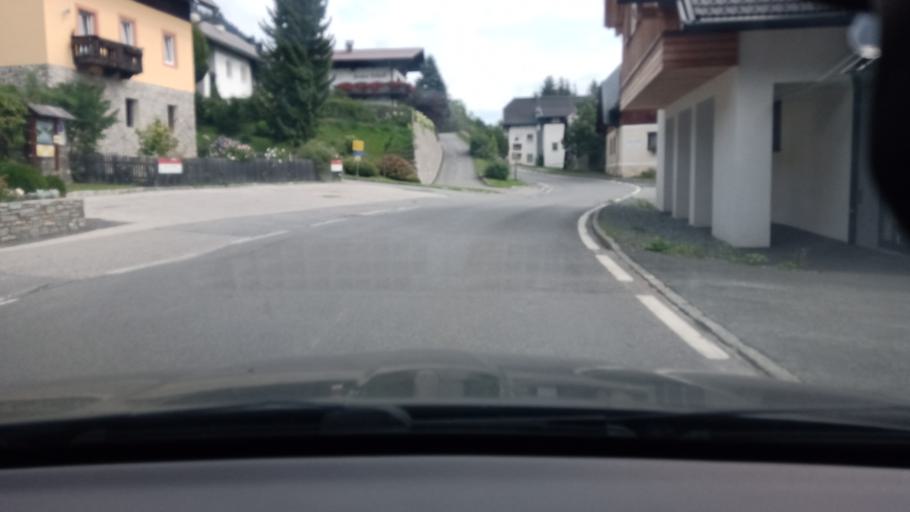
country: AT
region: Carinthia
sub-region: Politischer Bezirk Spittal an der Drau
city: Steinfeld
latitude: 46.7201
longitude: 13.2813
